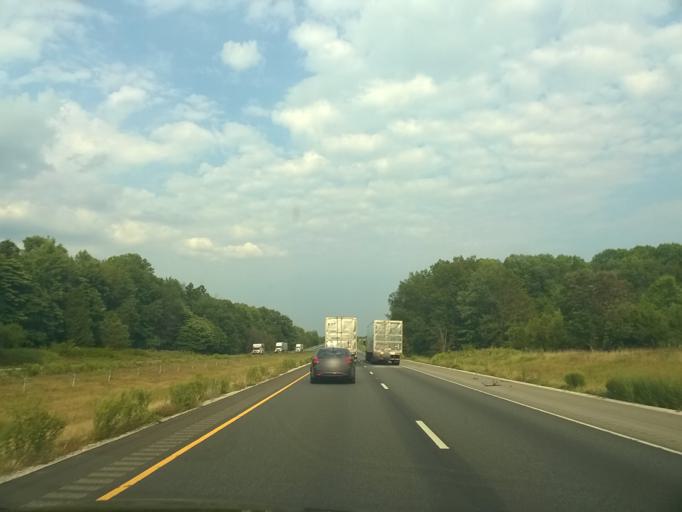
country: US
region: Indiana
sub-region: Clay County
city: Brazil
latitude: 39.4680
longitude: -87.0421
